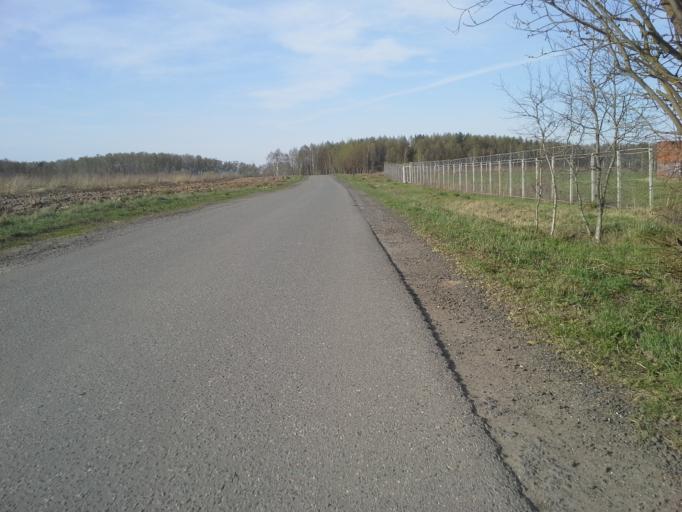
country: RU
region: Moskovskaya
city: Dubrovitsy
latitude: 55.4969
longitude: 37.4322
